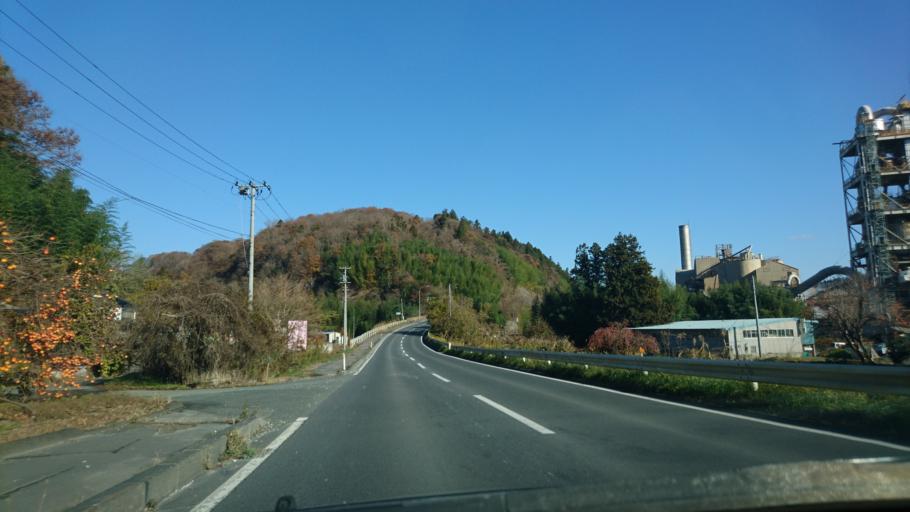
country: JP
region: Iwate
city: Ichinoseki
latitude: 38.9826
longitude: 141.2418
